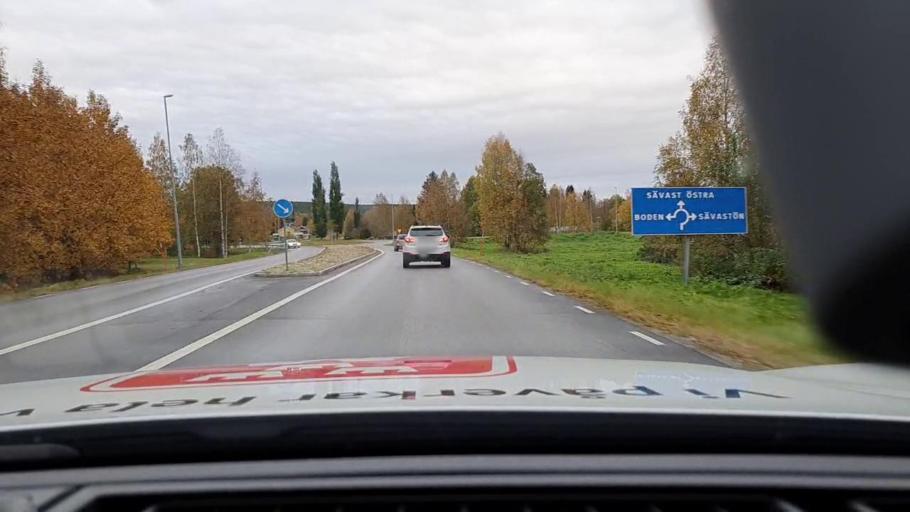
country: SE
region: Norrbotten
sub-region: Bodens Kommun
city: Saevast
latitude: 65.7688
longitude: 21.7375
